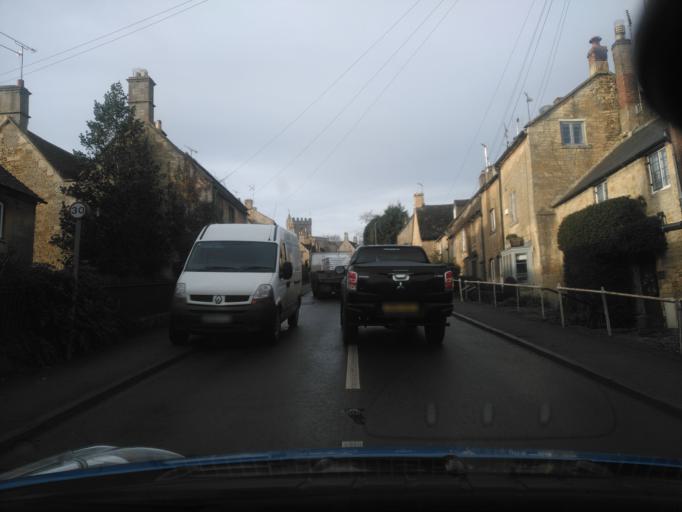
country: GB
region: England
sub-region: Gloucestershire
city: Moreton in Marsh
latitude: 51.9908
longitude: -1.7439
